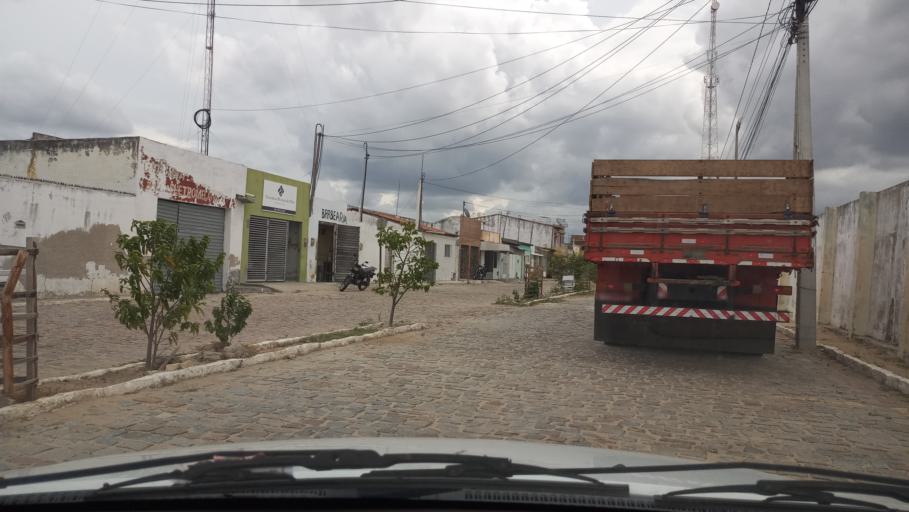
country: BR
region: Rio Grande do Norte
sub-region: Tangara
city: Tangara
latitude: -6.1969
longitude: -35.7996
